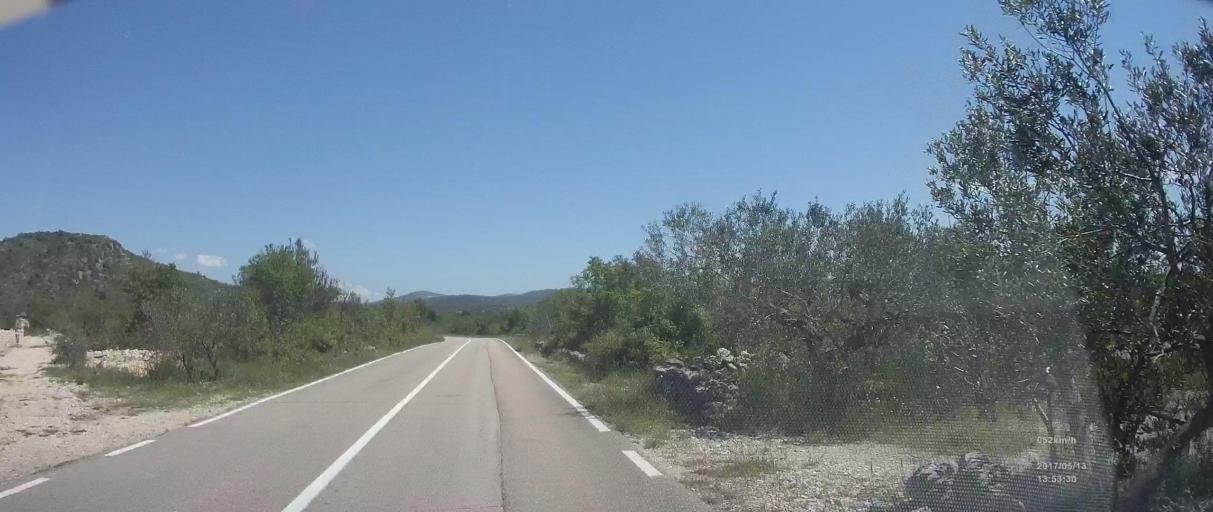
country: HR
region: Sibensko-Kniniska
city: Primosten
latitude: 43.5992
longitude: 15.9987
